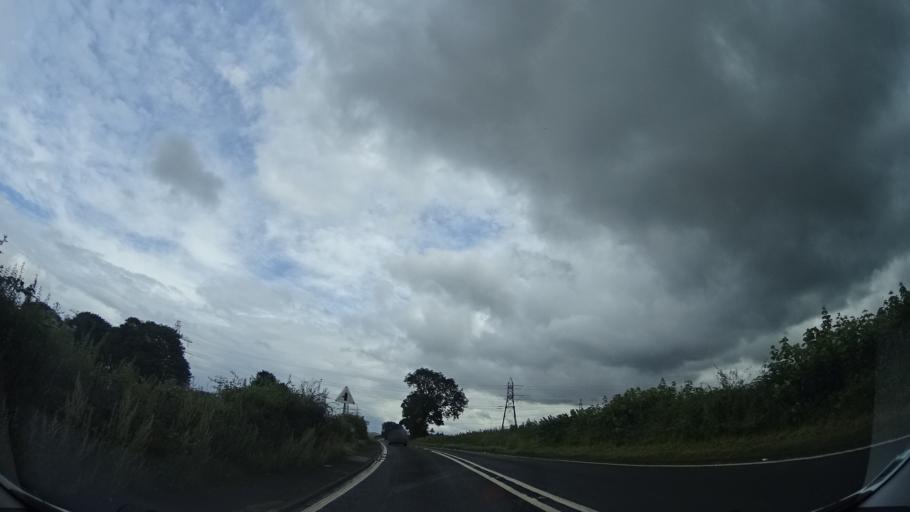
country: GB
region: Scotland
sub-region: Falkirk
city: Bonnybridge
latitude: 56.0057
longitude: -3.8632
